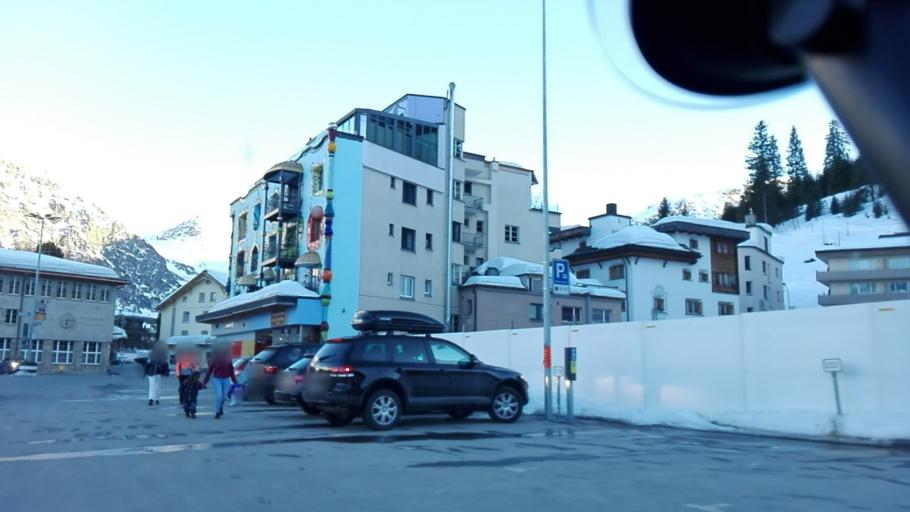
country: CH
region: Grisons
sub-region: Plessur District
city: Arosa
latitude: 46.7830
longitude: 9.6796
